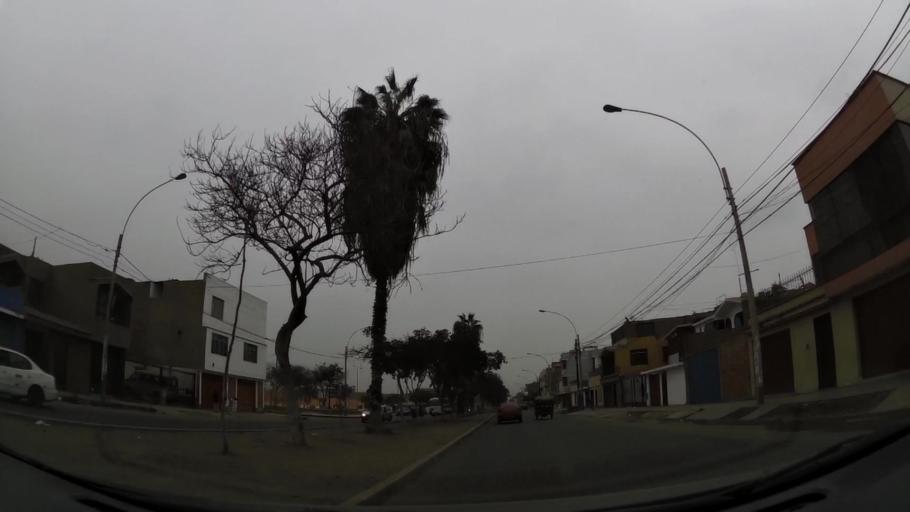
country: PE
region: Lima
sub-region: Lima
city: Urb. Santo Domingo
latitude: -11.9296
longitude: -77.0566
